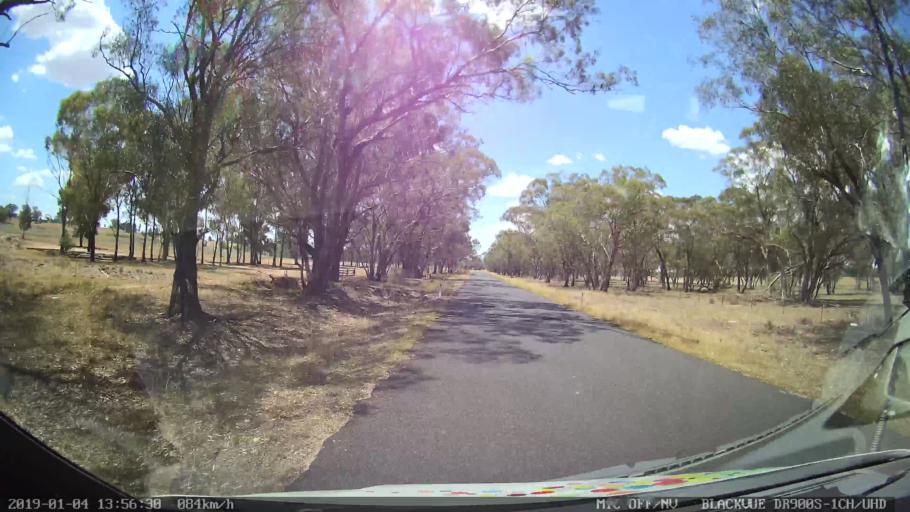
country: AU
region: New South Wales
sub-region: Dubbo Municipality
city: Dubbo
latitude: -32.3505
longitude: 148.5945
